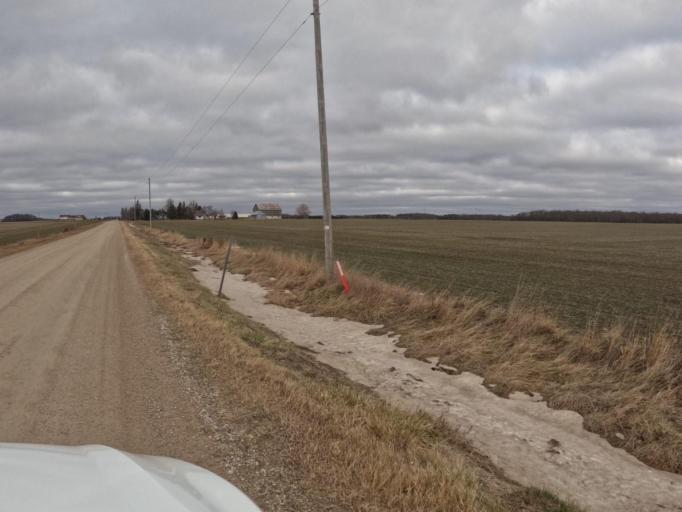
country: CA
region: Ontario
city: Shelburne
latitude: 43.8569
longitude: -80.3988
